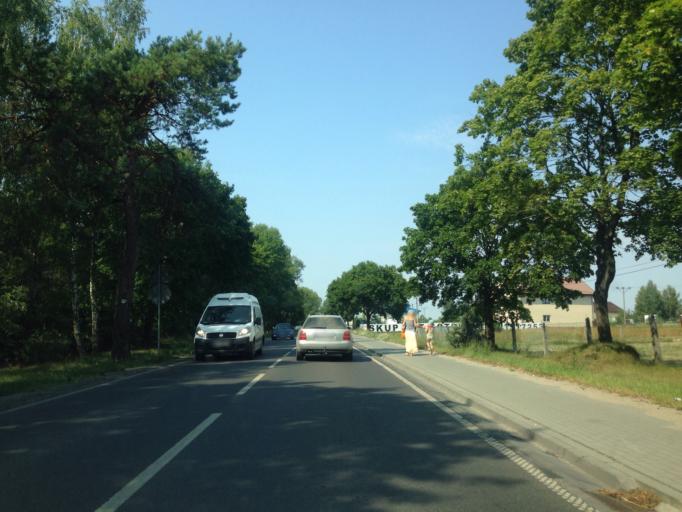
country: PL
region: Kujawsko-Pomorskie
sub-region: Powiat golubsko-dobrzynski
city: Golub-Dobrzyn
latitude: 53.1091
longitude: 19.0904
